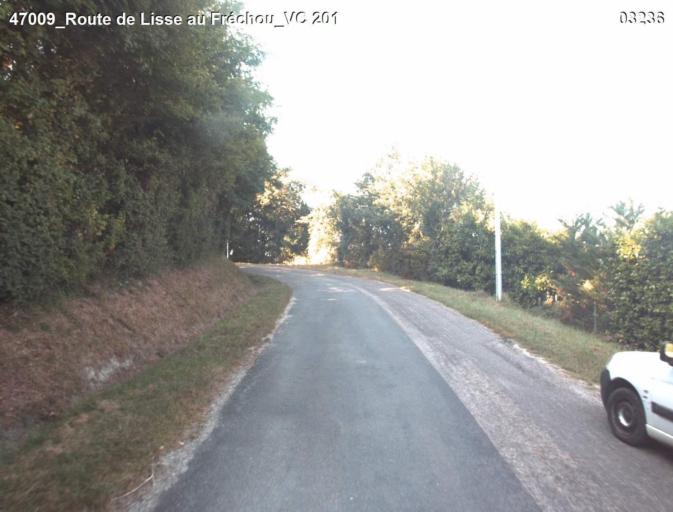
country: FR
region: Aquitaine
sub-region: Departement du Lot-et-Garonne
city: Mezin
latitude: 44.0983
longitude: 0.2746
